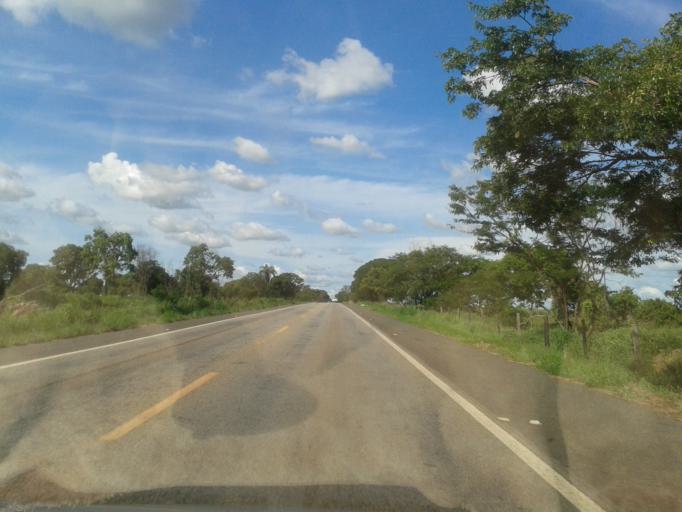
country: BR
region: Goias
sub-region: Mozarlandia
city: Mozarlandia
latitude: -15.0600
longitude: -50.6135
